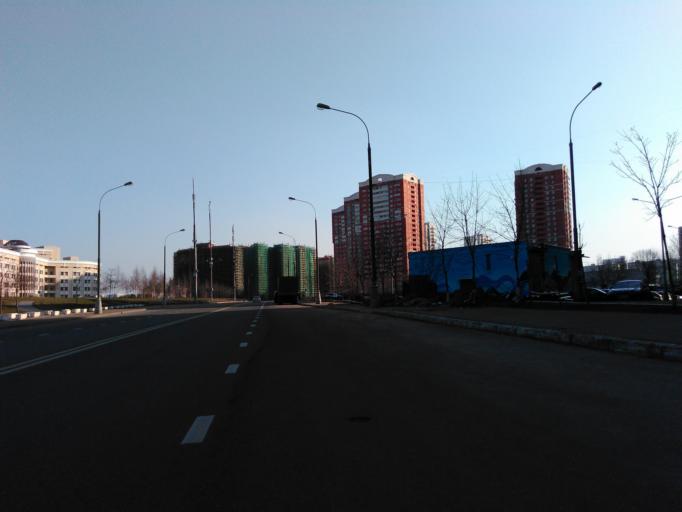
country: RU
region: Moscow
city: Ramenki
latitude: 55.7011
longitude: 37.5139
